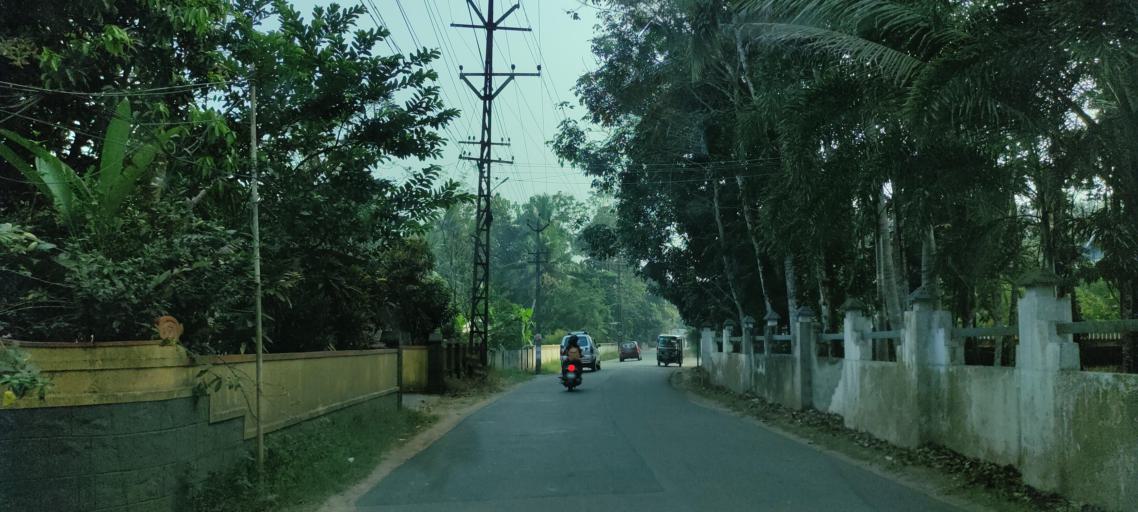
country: IN
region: Kerala
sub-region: Kottayam
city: Vaikam
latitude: 9.7194
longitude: 76.4766
